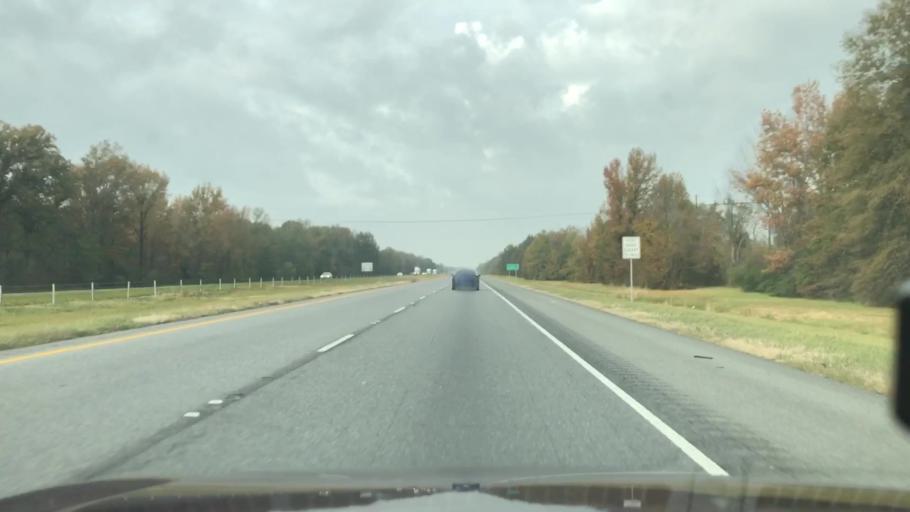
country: US
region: Louisiana
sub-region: Richland Parish
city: Delhi
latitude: 32.4450
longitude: -91.5069
